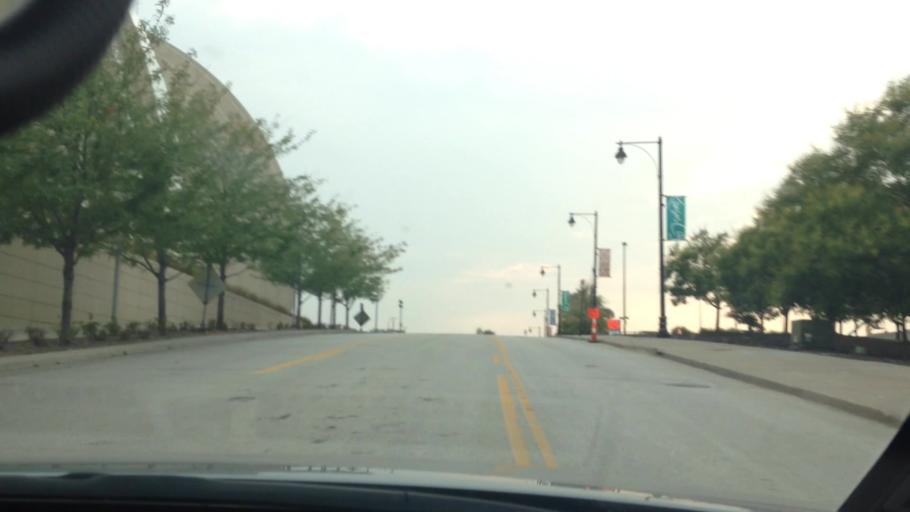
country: US
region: Missouri
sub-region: Jackson County
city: Kansas City
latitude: 39.0946
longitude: -94.5862
